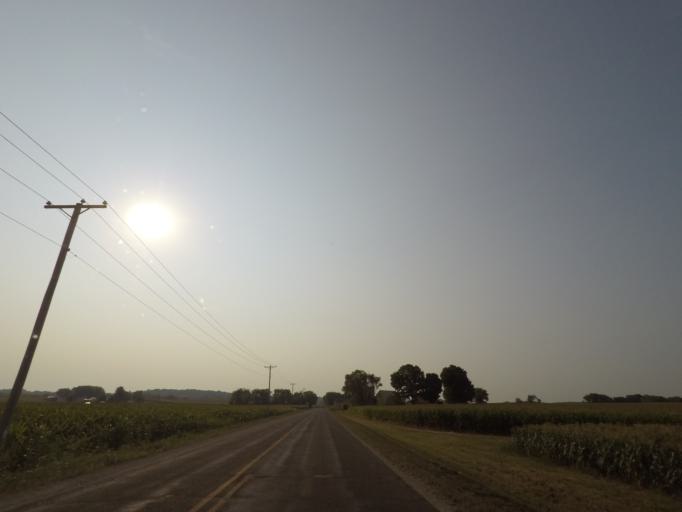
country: US
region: Wisconsin
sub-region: Dane County
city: Cottage Grove
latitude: 43.0504
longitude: -89.2437
